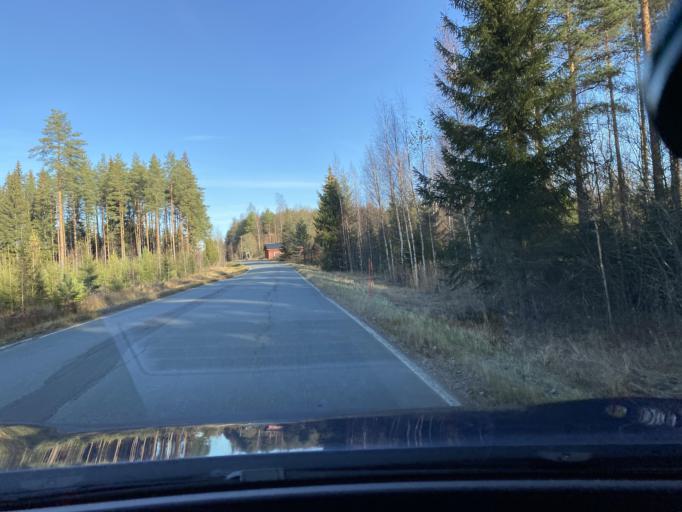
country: FI
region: Haeme
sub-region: Forssa
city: Tammela
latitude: 60.9055
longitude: 23.8558
